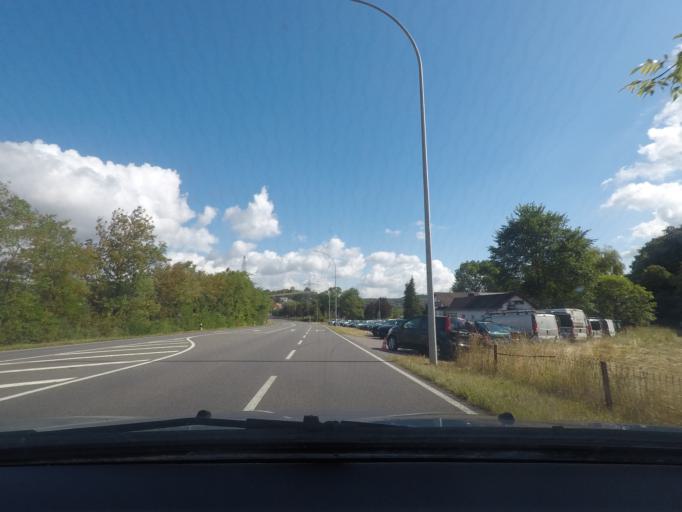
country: LU
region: Grevenmacher
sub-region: Canton de Grevenmacher
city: Junglinster
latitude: 49.7339
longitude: 6.2857
